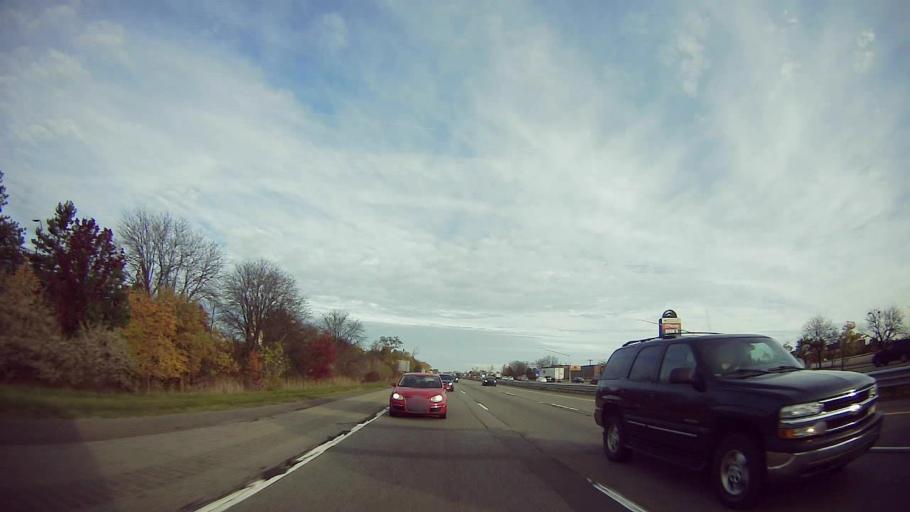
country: US
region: Michigan
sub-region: Oakland County
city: Clawson
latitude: 42.5384
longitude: -83.1165
